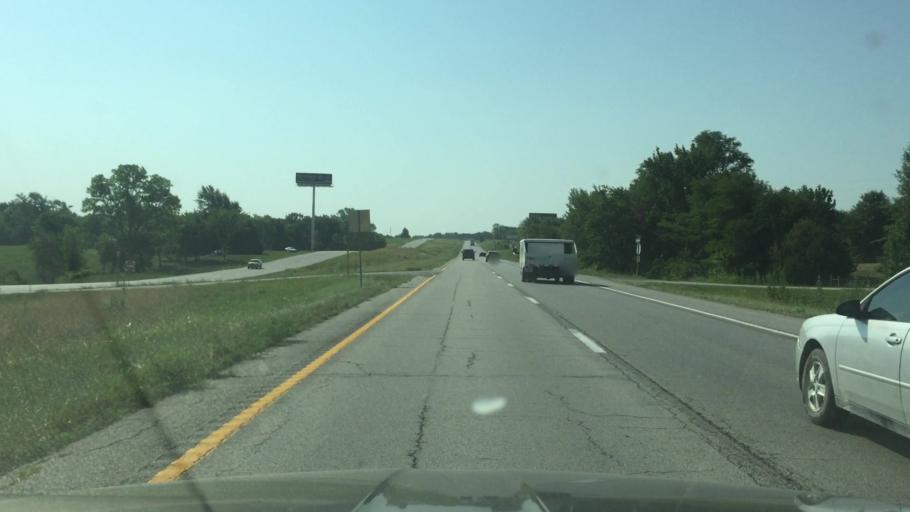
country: US
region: Missouri
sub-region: Johnson County
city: Holden
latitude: 38.8432
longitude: -93.9571
